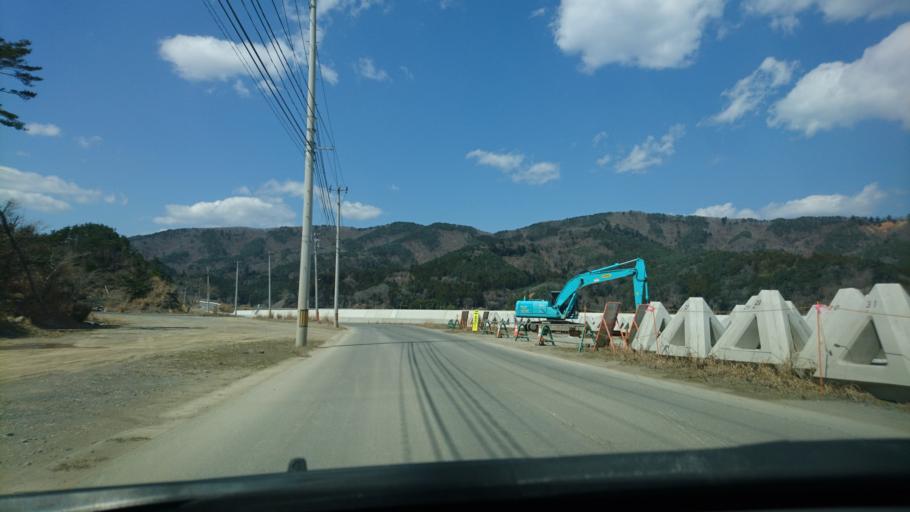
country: JP
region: Miyagi
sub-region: Oshika Gun
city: Onagawa Cho
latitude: 38.5148
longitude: 141.4773
